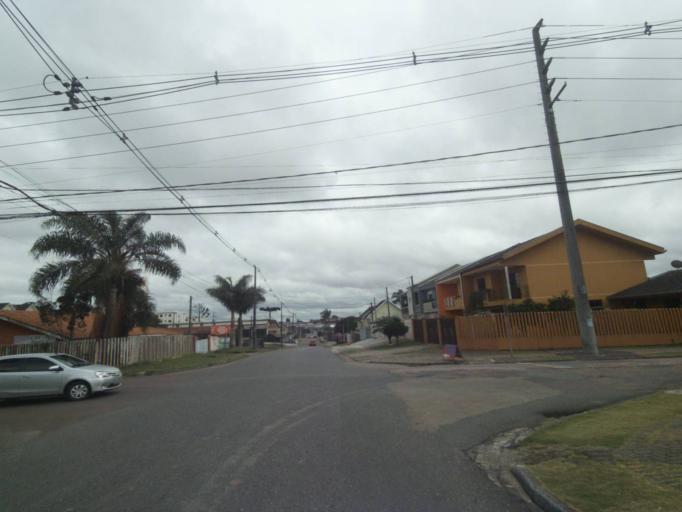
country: BR
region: Parana
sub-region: Sao Jose Dos Pinhais
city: Sao Jose dos Pinhais
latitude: -25.5309
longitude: -49.2905
